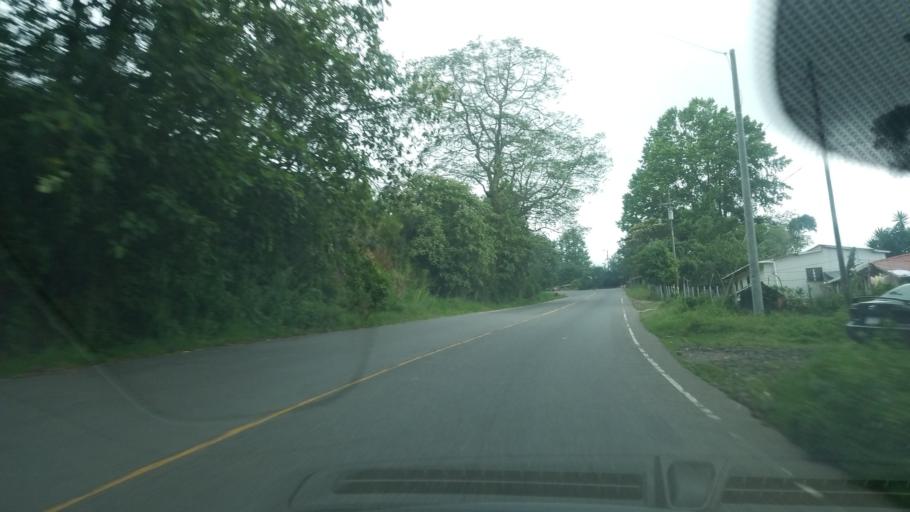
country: HN
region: Ocotepeque
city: La Labor
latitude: 14.4789
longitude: -89.0534
